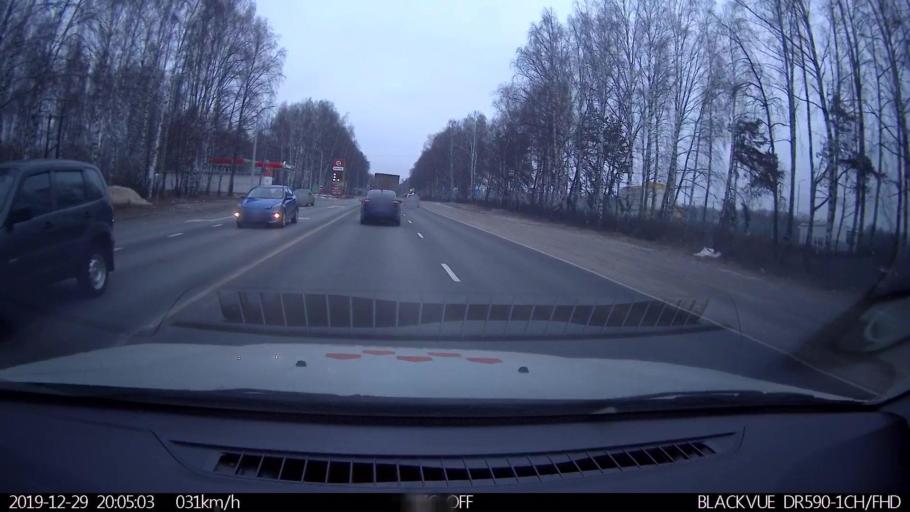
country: RU
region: Nizjnij Novgorod
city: Neklyudovo
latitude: 56.3884
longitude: 44.0111
